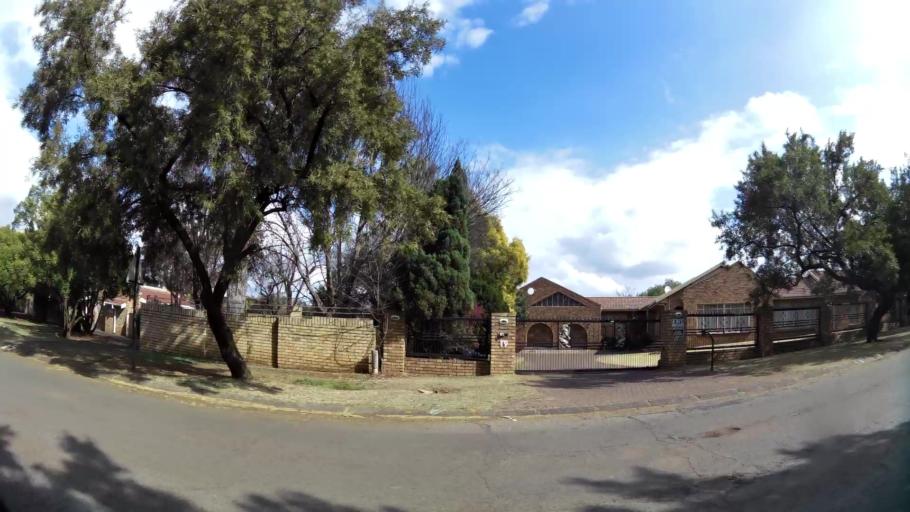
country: ZA
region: Gauteng
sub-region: Sedibeng District Municipality
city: Vanderbijlpark
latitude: -26.7411
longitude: 27.8256
